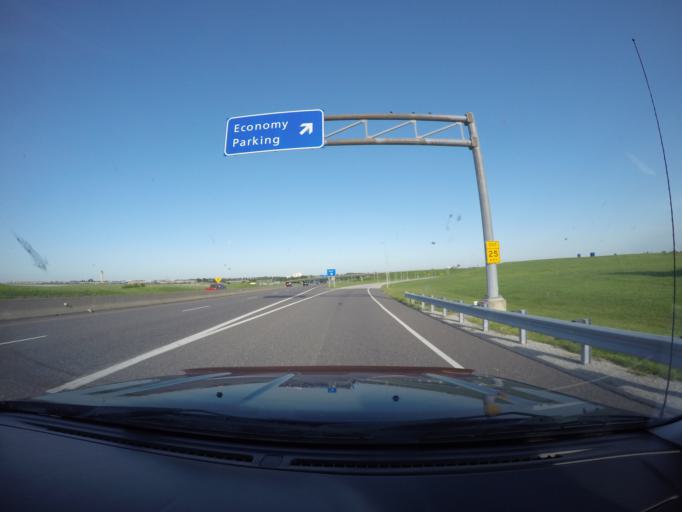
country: US
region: Missouri
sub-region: Platte County
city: Weatherby Lake
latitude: 39.3113
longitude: -94.6973
